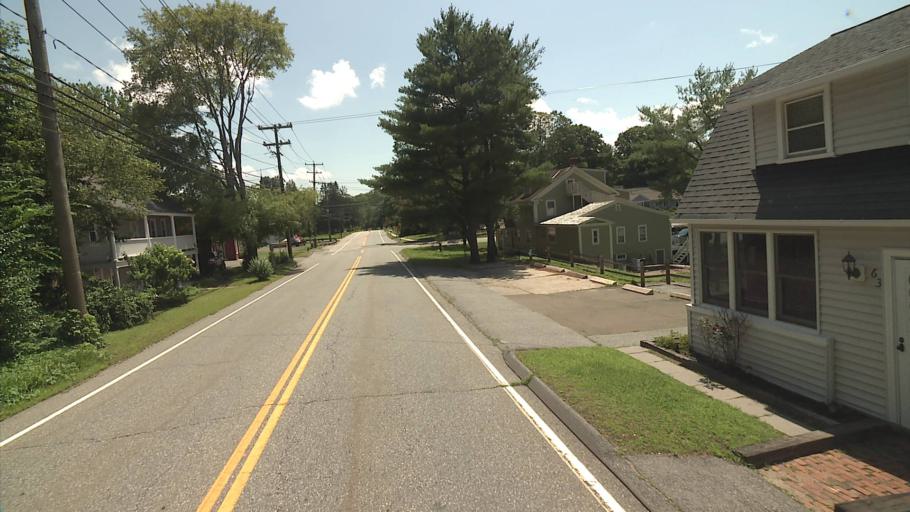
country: US
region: Connecticut
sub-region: Middlesex County
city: Chester Center
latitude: 41.4026
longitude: -72.4421
